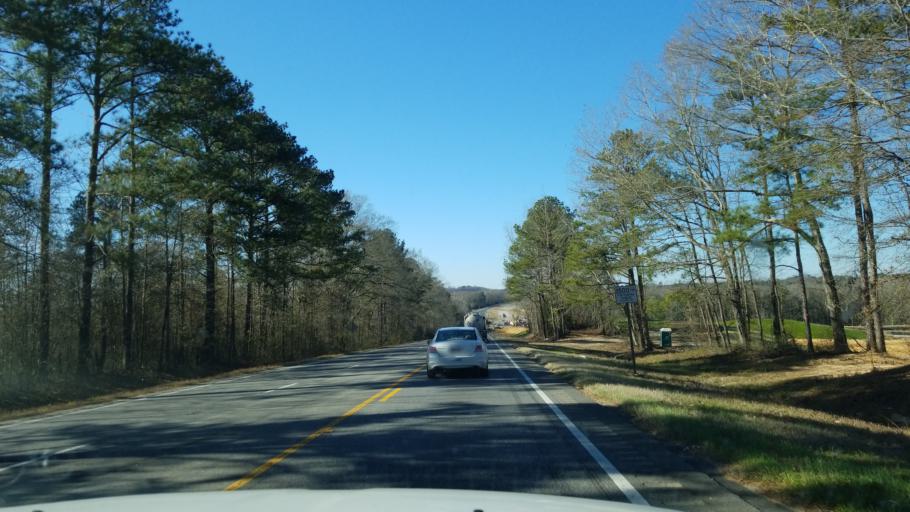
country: US
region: Alabama
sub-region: Pickens County
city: Gordo
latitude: 33.3330
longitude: -87.9199
